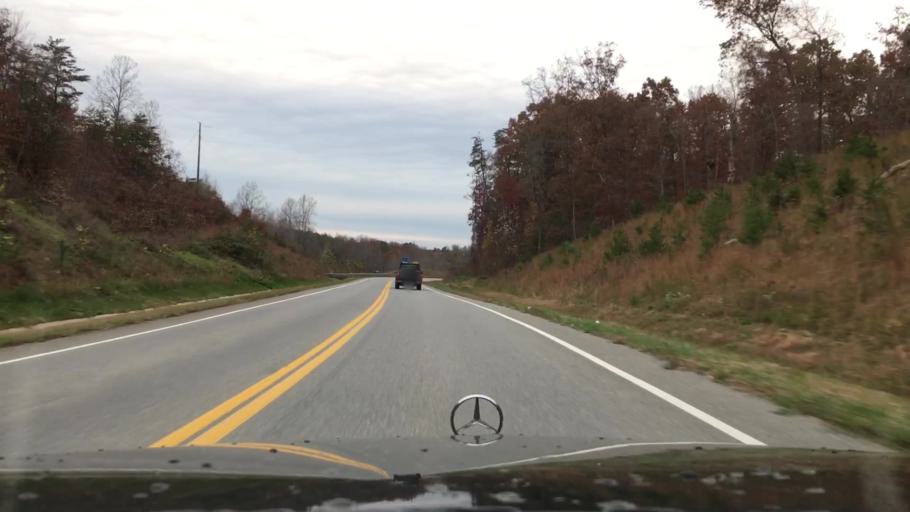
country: US
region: Virginia
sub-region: Campbell County
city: Altavista
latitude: 37.1851
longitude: -79.2930
